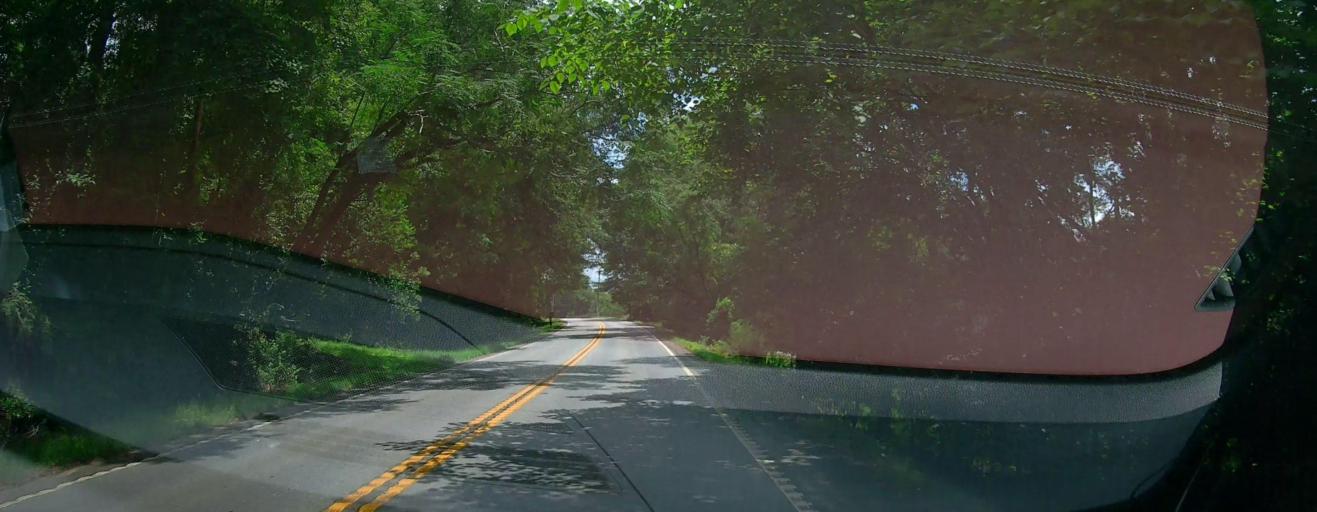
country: US
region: Georgia
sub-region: Houston County
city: Robins Air Force Base
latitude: 32.4987
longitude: -83.6151
